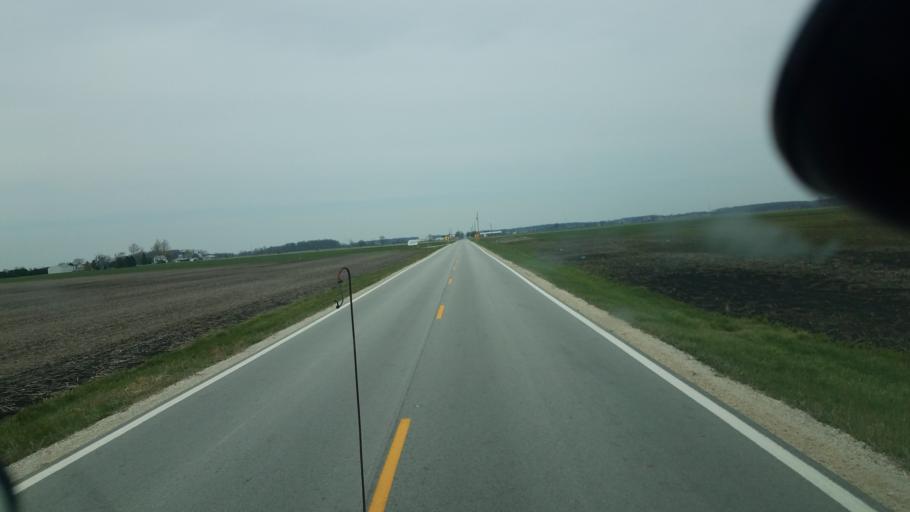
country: US
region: Ohio
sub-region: Wyandot County
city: Carey
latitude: 40.9969
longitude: -83.4778
